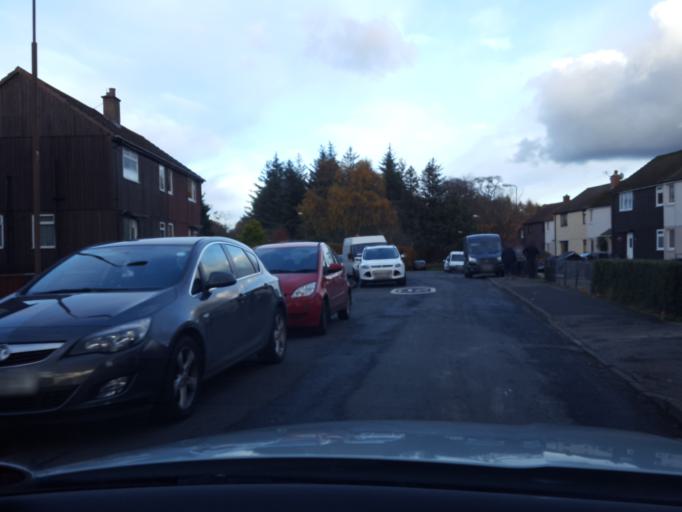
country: GB
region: Scotland
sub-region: West Lothian
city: West Calder
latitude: 55.8584
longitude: -3.5504
